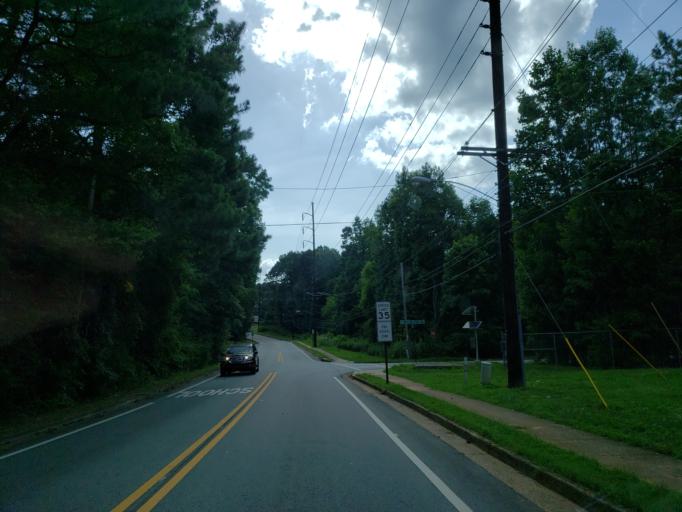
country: US
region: Georgia
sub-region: Cobb County
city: Powder Springs
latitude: 33.8753
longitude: -84.6701
